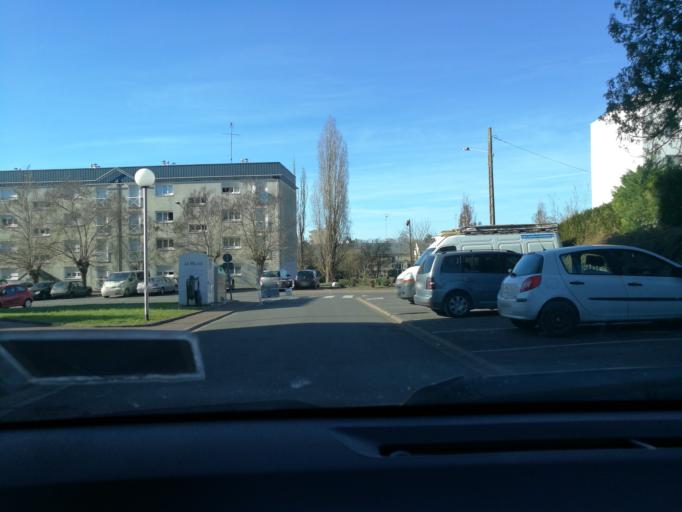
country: FR
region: Centre
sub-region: Departement du Loiret
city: Saint-Jean-de-la-Ruelle
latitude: 47.9046
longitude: 1.8766
